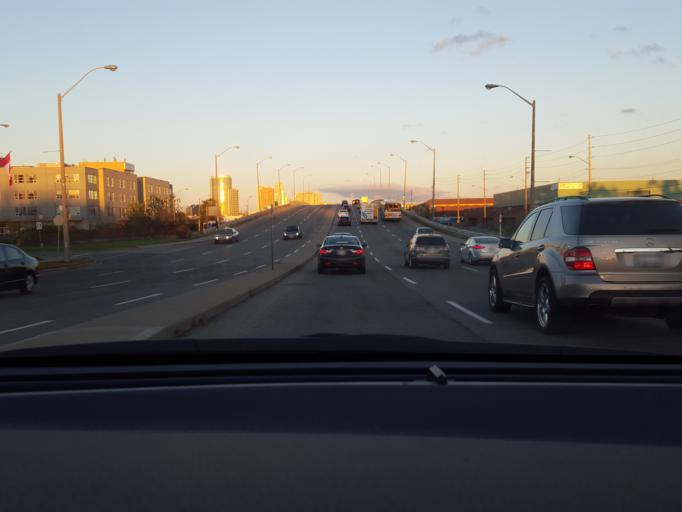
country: CA
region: Ontario
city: Scarborough
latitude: 43.7661
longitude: -79.2797
